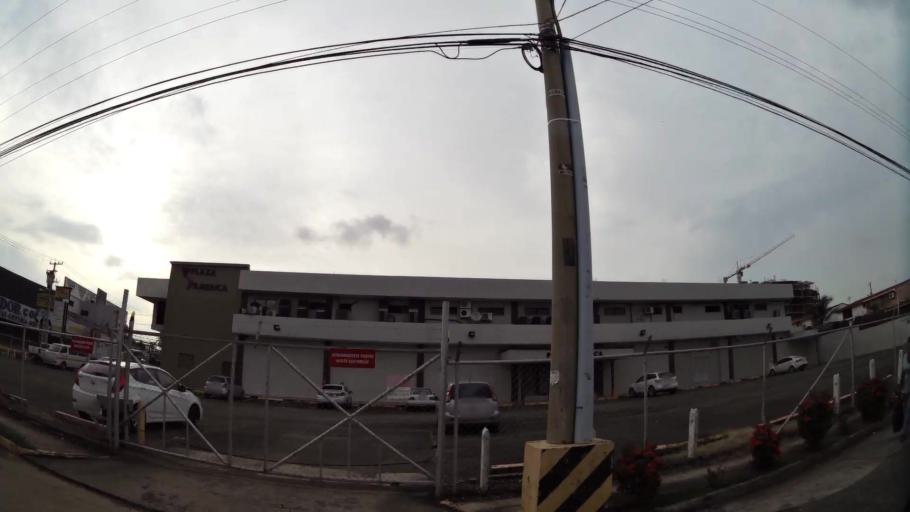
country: PA
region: Panama
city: Panama
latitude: 9.0013
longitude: -79.5185
